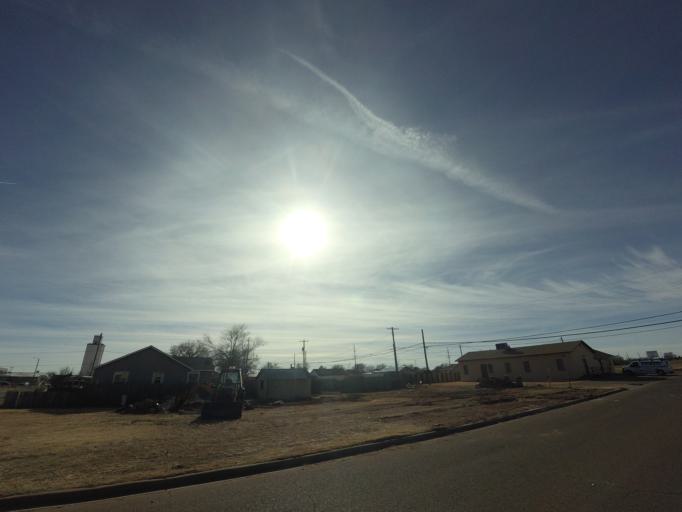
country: US
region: New Mexico
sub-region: Curry County
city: Clovis
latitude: 34.4018
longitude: -103.2219
